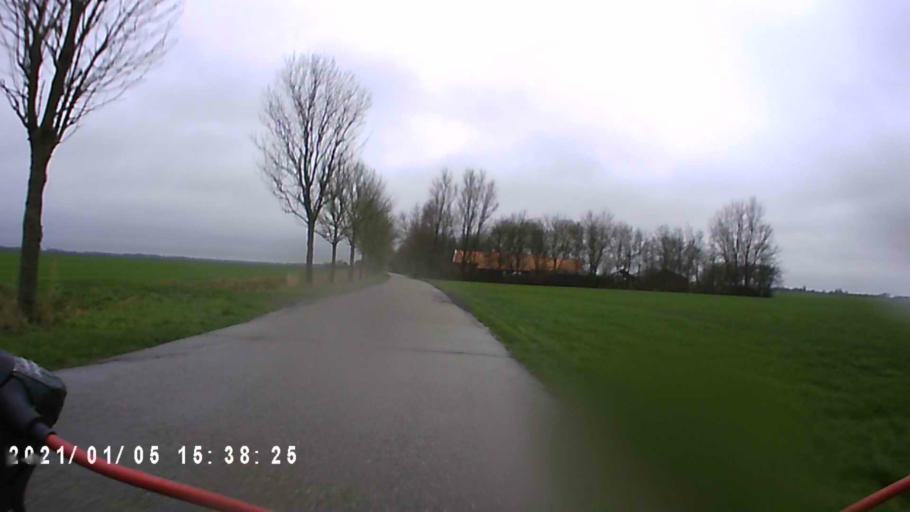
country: DE
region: Lower Saxony
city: Bunde
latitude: 53.2133
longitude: 7.1581
